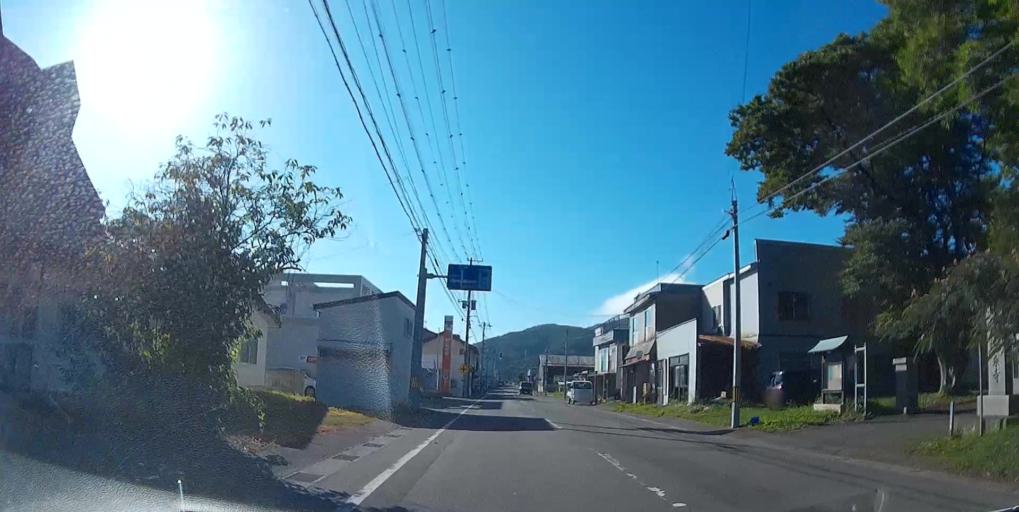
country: JP
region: Hokkaido
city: Kamiiso
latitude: 42.2261
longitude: 139.8197
